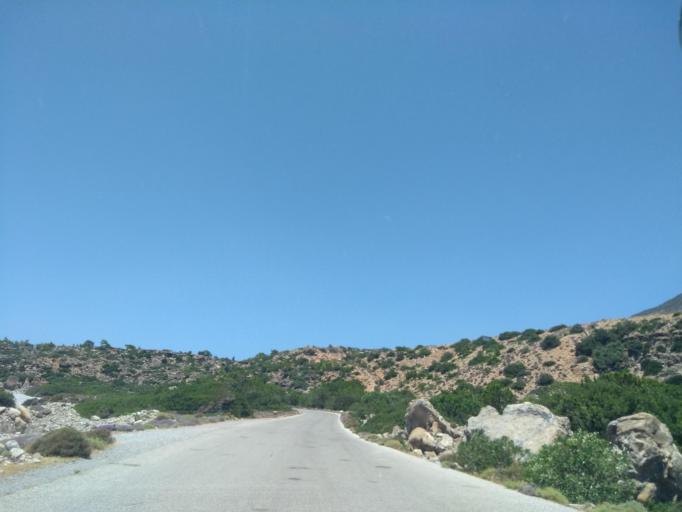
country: GR
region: Crete
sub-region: Nomos Chanias
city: Vryses
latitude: 35.3284
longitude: 23.5488
